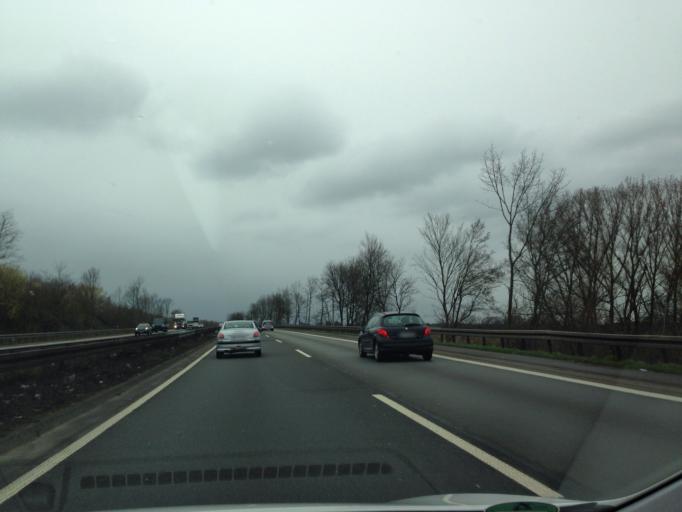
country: DE
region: North Rhine-Westphalia
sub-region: Regierungsbezirk Dusseldorf
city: Krefeld
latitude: 51.3804
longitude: 6.6175
